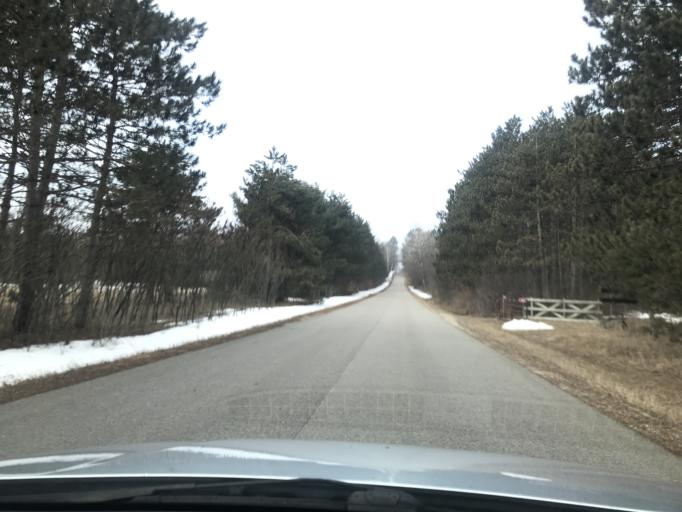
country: US
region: Wisconsin
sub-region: Oconto County
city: Oconto Falls
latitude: 44.8295
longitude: -88.1768
